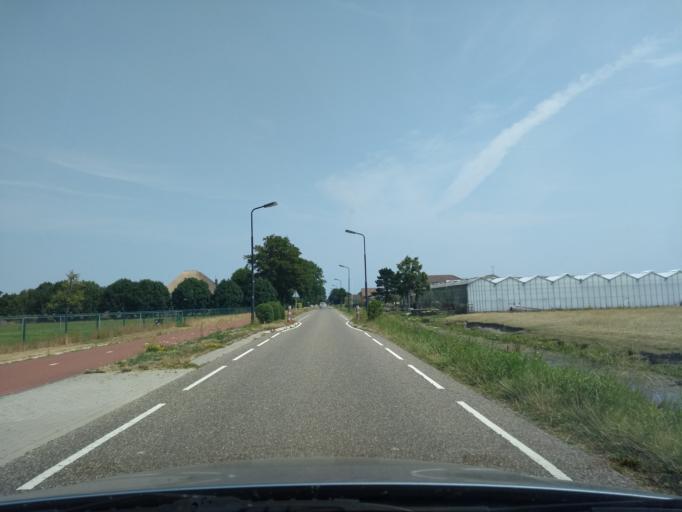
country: NL
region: North Holland
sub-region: Gemeente Langedijk
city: Broek op Langedijk
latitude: 52.6388
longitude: 4.8228
